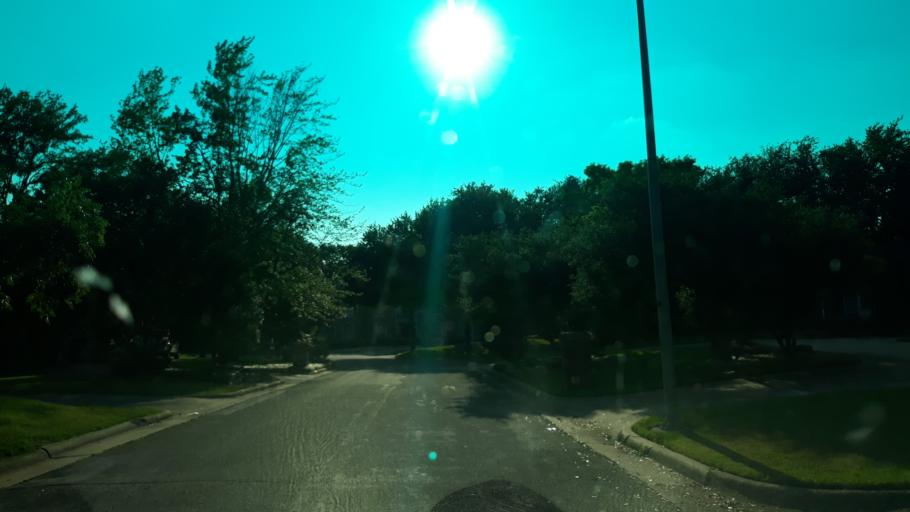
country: US
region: Texas
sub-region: Dallas County
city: Addison
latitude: 32.9484
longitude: -96.7967
